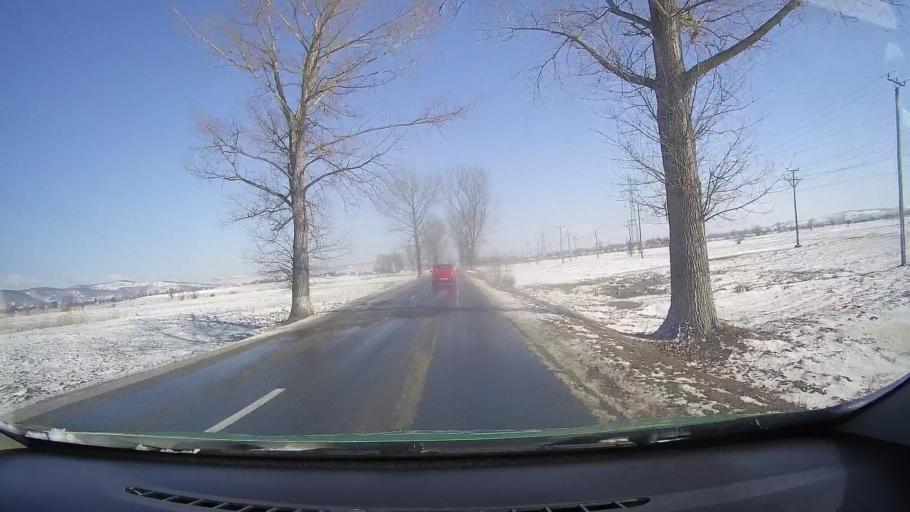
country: RO
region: Sibiu
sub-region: Comuna Avrig
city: Marsa
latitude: 45.7128
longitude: 24.3699
